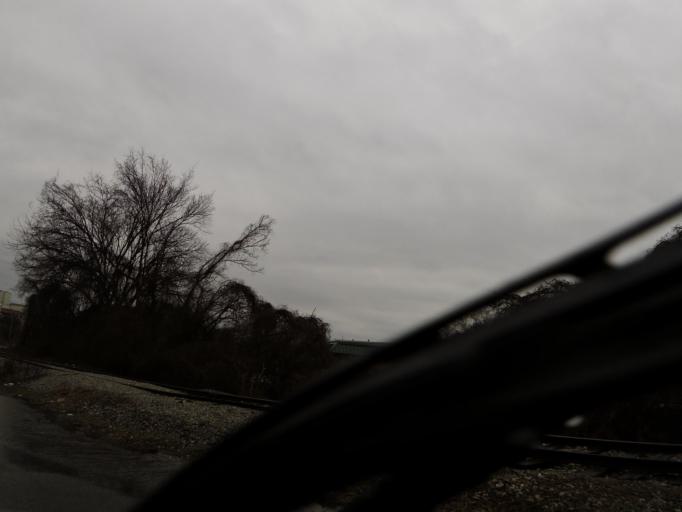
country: US
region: Tennessee
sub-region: Knox County
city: Knoxville
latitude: 35.9693
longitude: -83.9539
